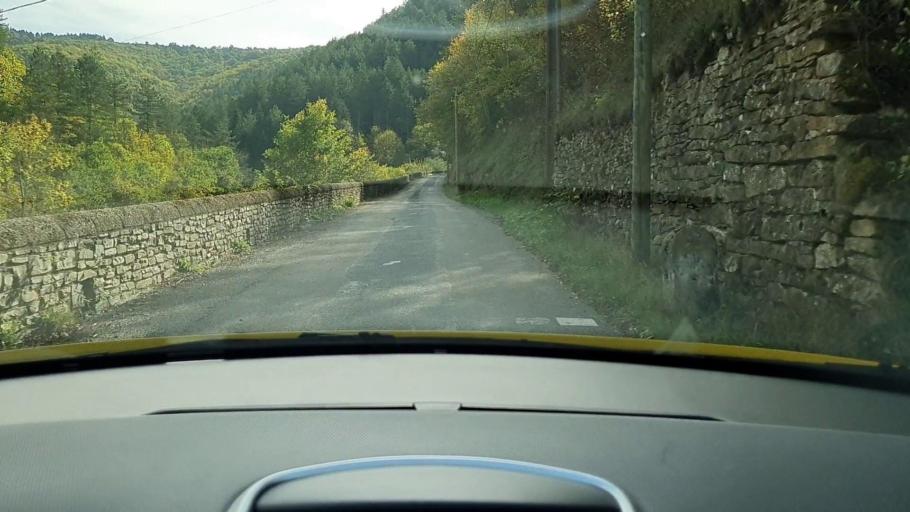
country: FR
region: Languedoc-Roussillon
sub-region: Departement de la Lozere
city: Meyrueis
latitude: 44.0749
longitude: 3.3901
